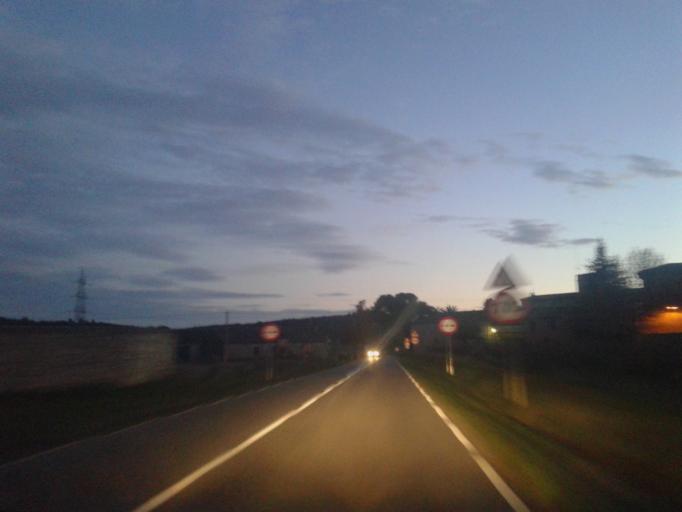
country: ES
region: Catalonia
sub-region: Provincia de Barcelona
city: Avinyonet del Penedes
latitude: 41.3428
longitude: 1.7442
